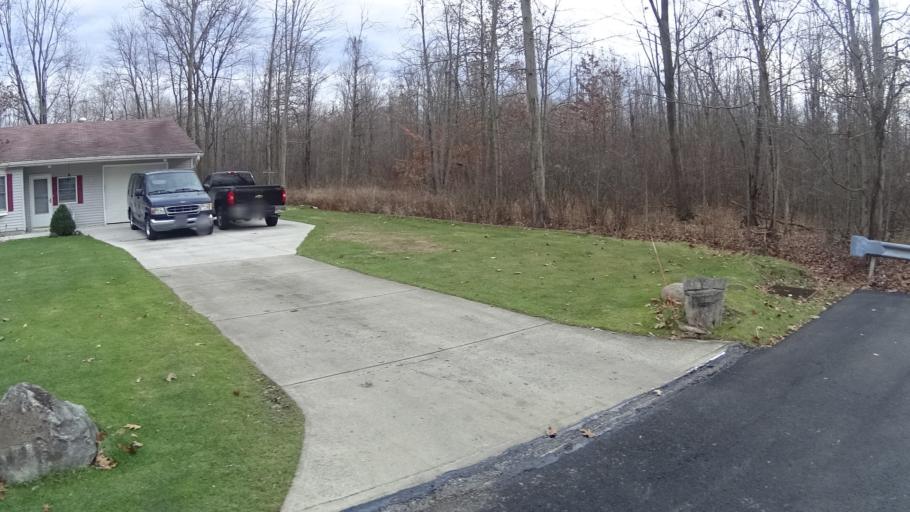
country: US
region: Ohio
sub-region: Lorain County
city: Eaton Estates
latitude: 41.3065
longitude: -81.9421
